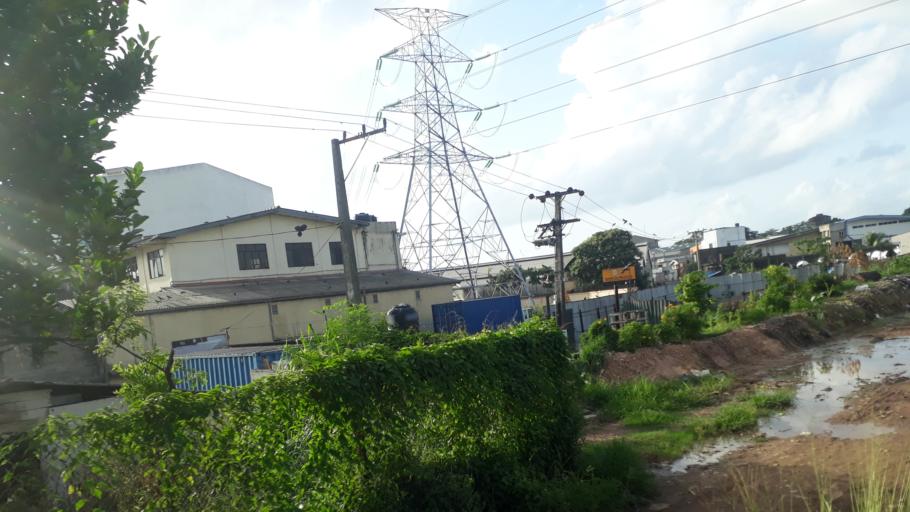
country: LK
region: Western
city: Kolonnawa
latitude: 6.9440
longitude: 79.8847
